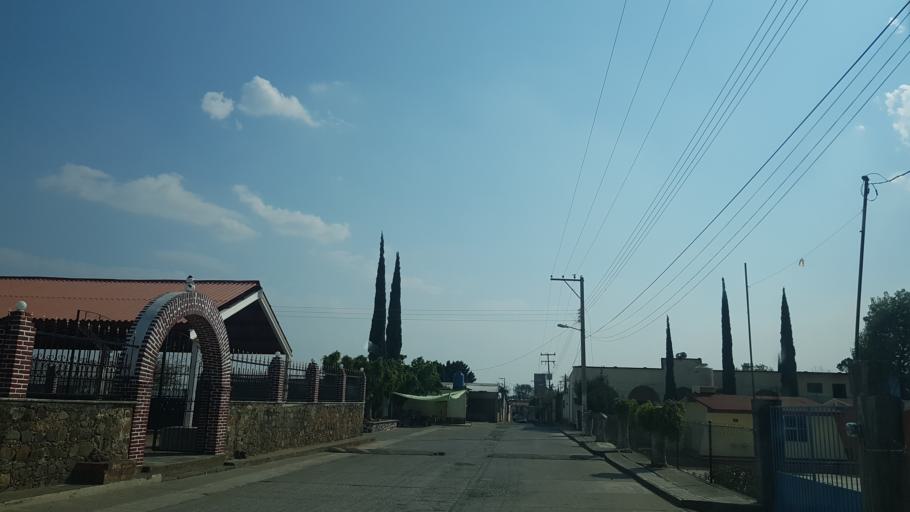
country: MX
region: Morelos
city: Tlacotepec
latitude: 18.8111
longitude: -98.7115
